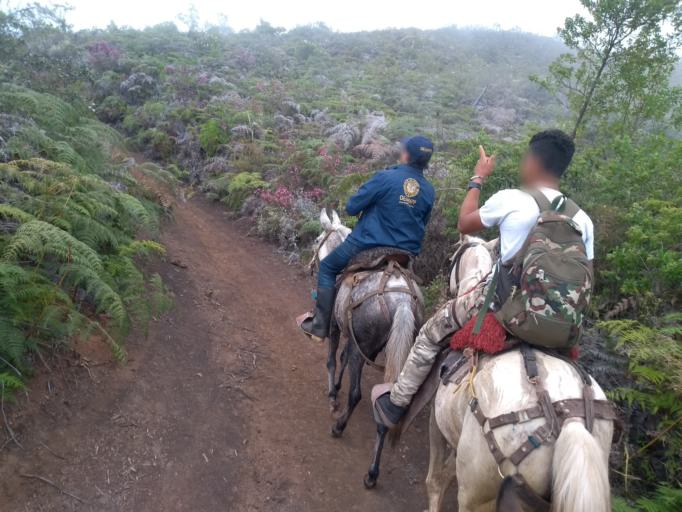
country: CO
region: Cesar
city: San Diego
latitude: 10.1799
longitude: -73.0422
